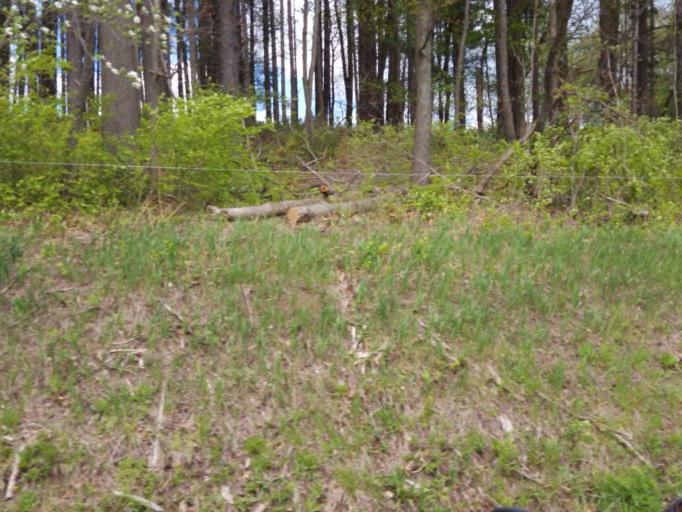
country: US
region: Ohio
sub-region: Ashland County
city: Loudonville
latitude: 40.5488
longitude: -82.2400
